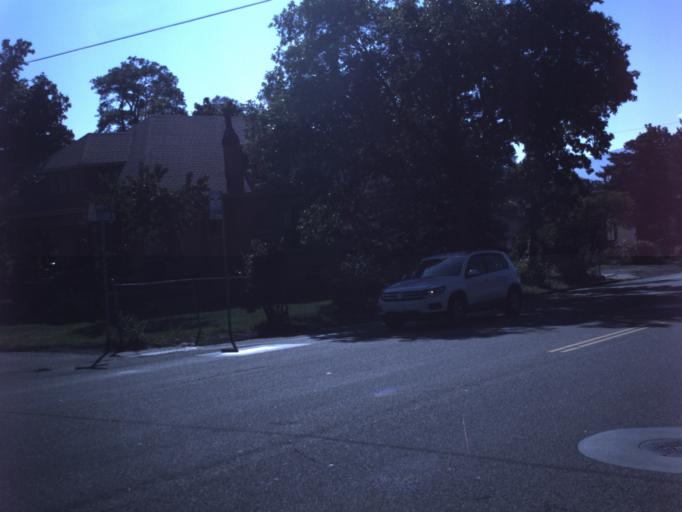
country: US
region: Utah
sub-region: Salt Lake County
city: East Millcreek
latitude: 40.6999
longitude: -111.8171
